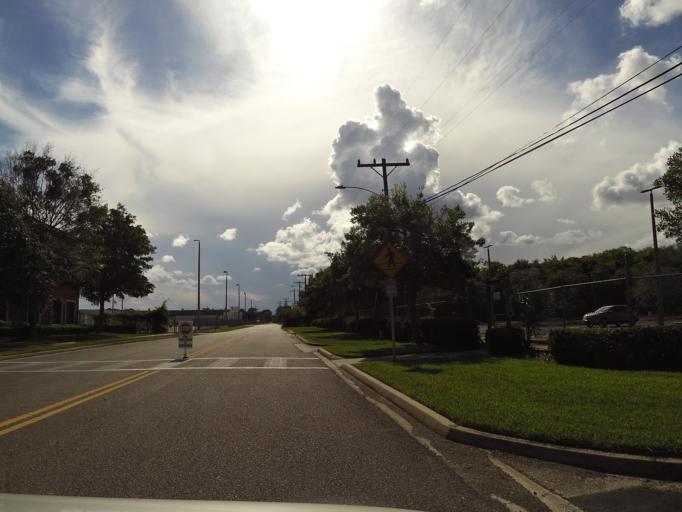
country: US
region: Florida
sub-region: Duval County
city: Jacksonville
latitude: 30.3252
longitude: -81.7323
